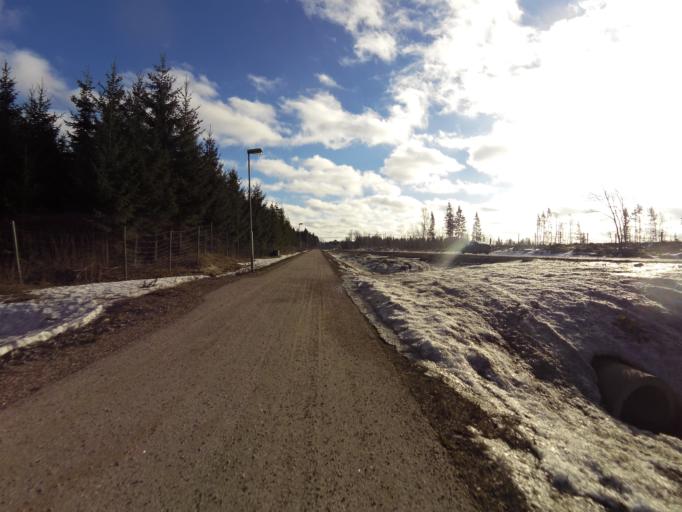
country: SE
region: Gaevleborg
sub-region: Gavle Kommun
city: Gavle
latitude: 60.6480
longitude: 17.2499
